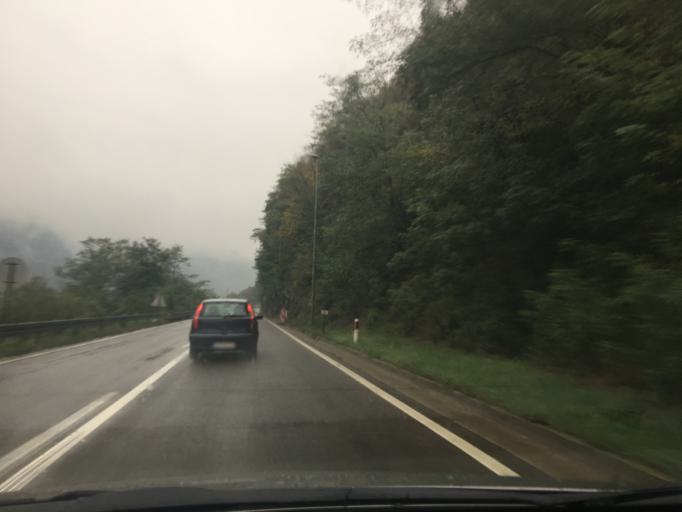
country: RS
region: Central Serbia
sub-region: Pcinjski Okrug
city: Vladicin Han
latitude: 42.7455
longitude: 22.0642
